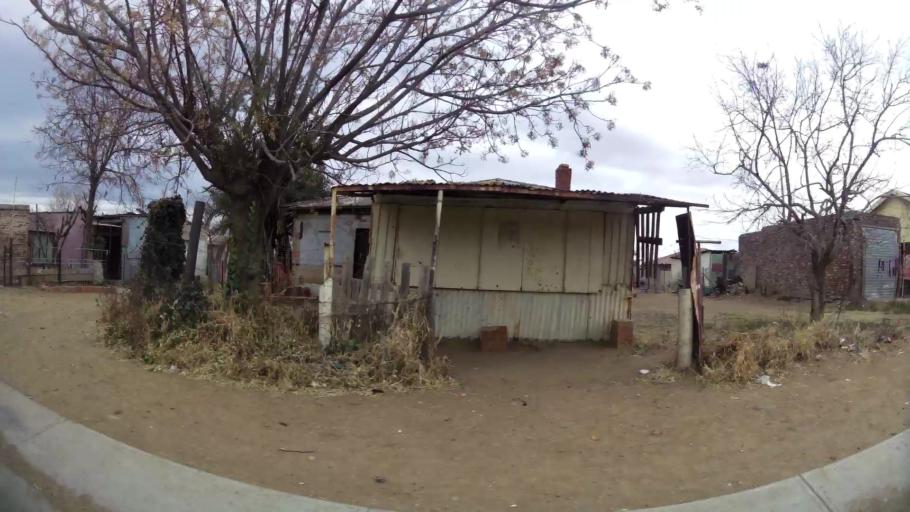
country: ZA
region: Orange Free State
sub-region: Fezile Dabi District Municipality
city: Kroonstad
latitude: -27.6509
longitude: 27.2024
